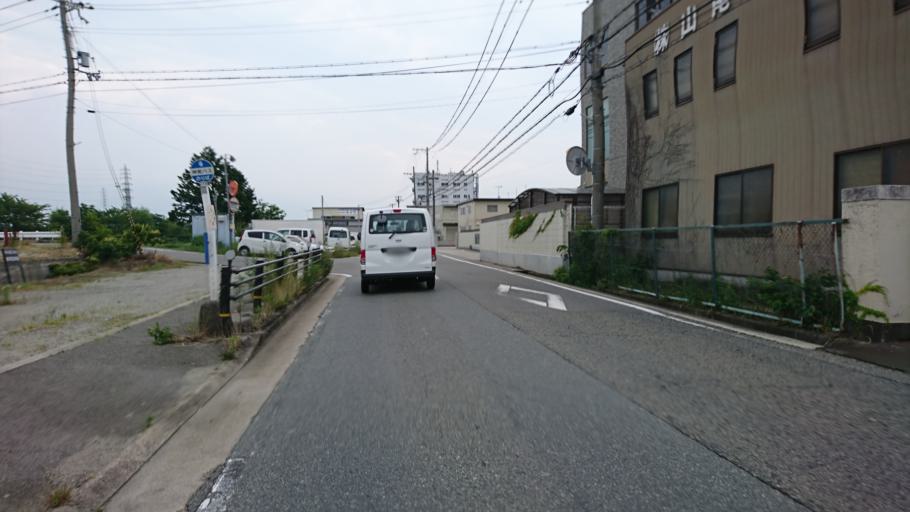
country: JP
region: Hyogo
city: Miki
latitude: 34.7303
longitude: 134.9181
